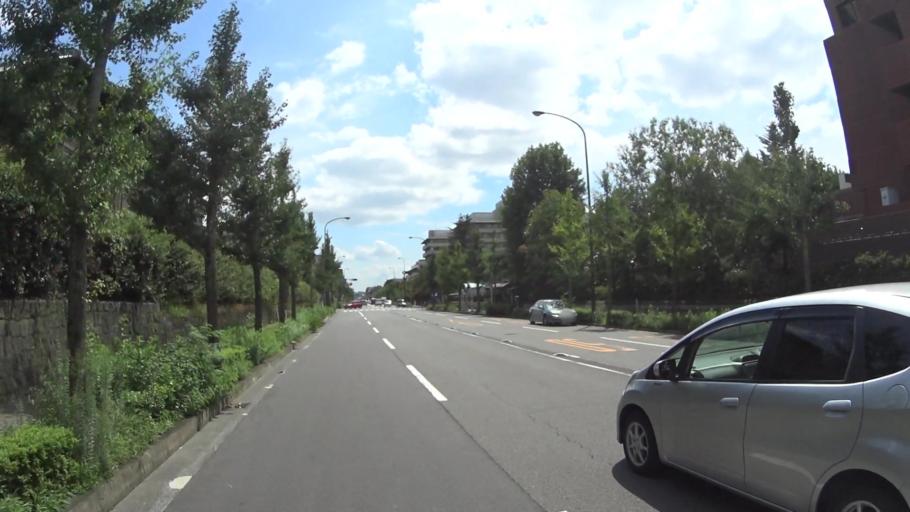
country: JP
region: Kyoto
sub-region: Kyoto-shi
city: Kamigyo-ku
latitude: 35.0231
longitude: 135.7786
